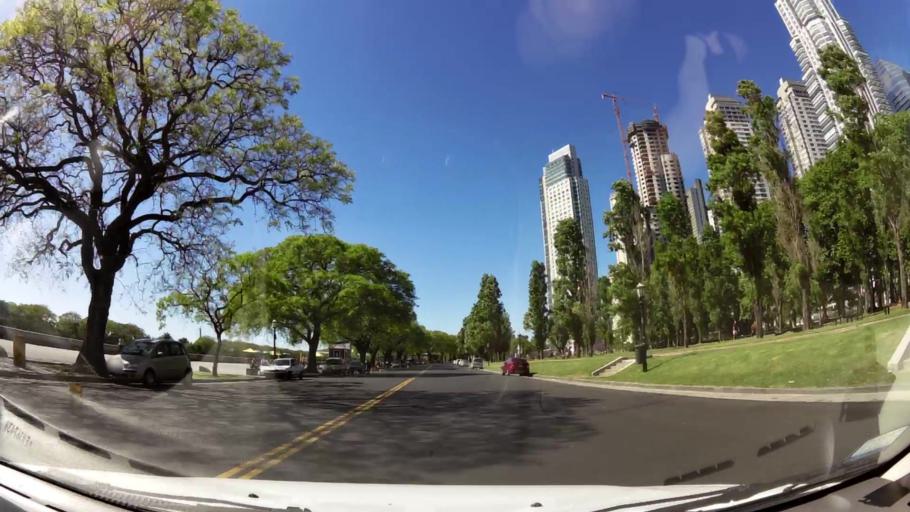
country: AR
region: Buenos Aires F.D.
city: Buenos Aires
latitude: -34.6092
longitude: -58.3592
